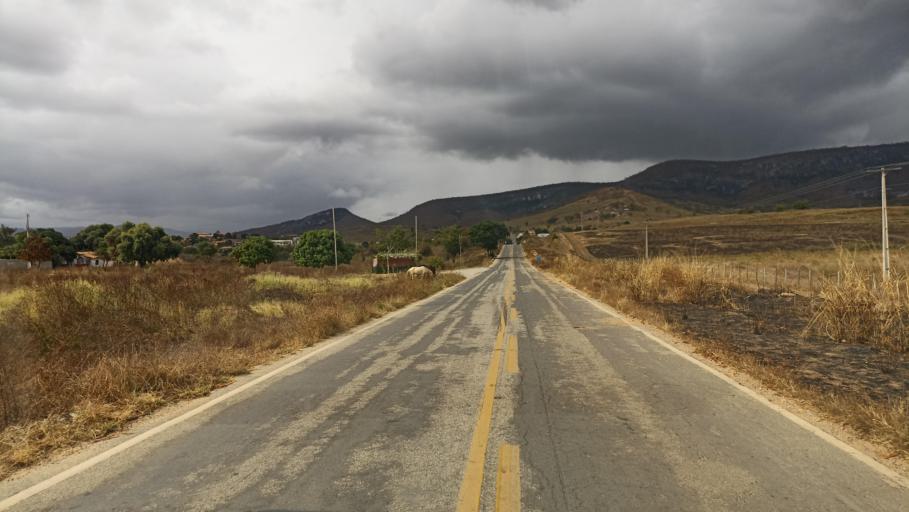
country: BR
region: Minas Gerais
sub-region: Itinga
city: Itinga
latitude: -16.6203
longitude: -41.7709
